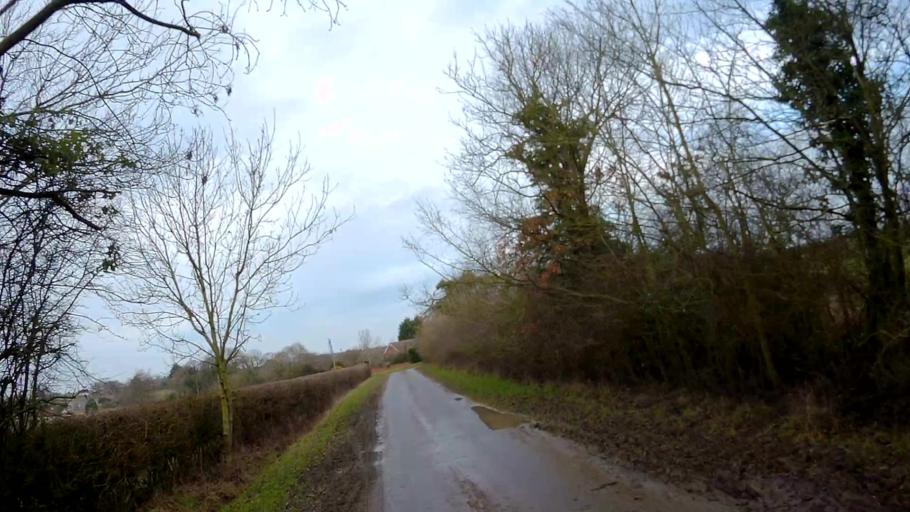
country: GB
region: England
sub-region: Lincolnshire
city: Bourne
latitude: 52.8202
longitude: -0.4381
